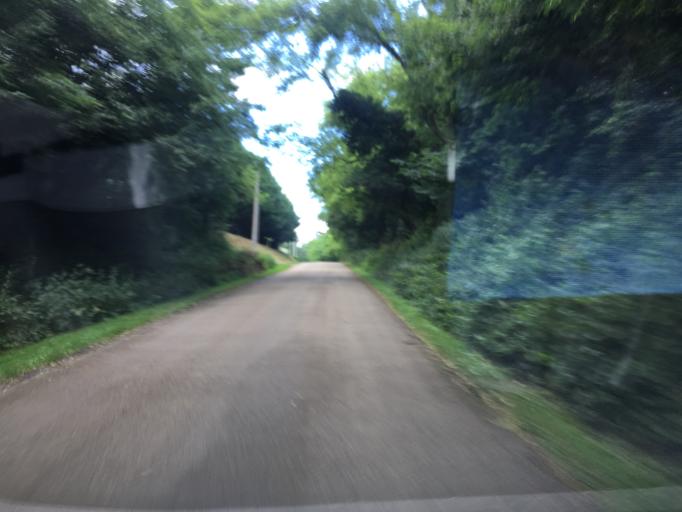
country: FR
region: Bourgogne
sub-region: Departement de l'Yonne
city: Fleury-la-Vallee
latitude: 47.8686
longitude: 3.4814
